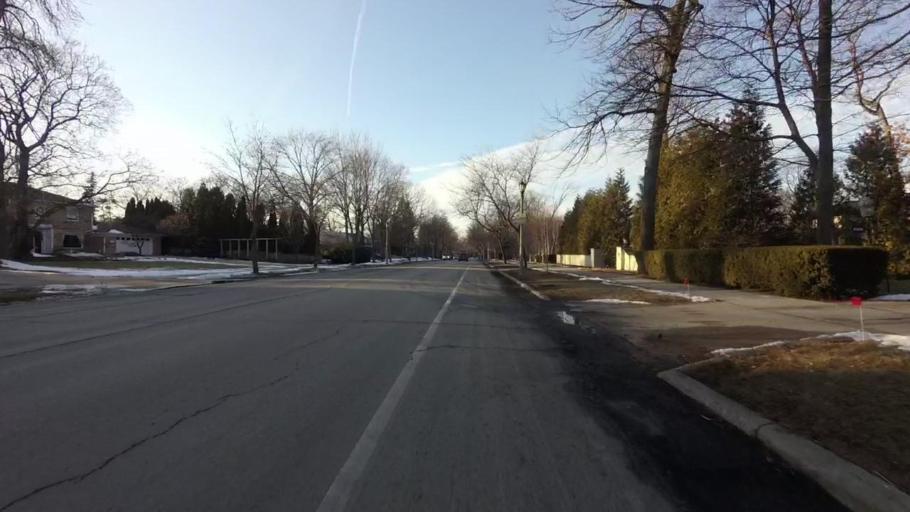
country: US
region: Wisconsin
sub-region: Milwaukee County
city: Shorewood
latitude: 43.1000
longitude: -87.8803
